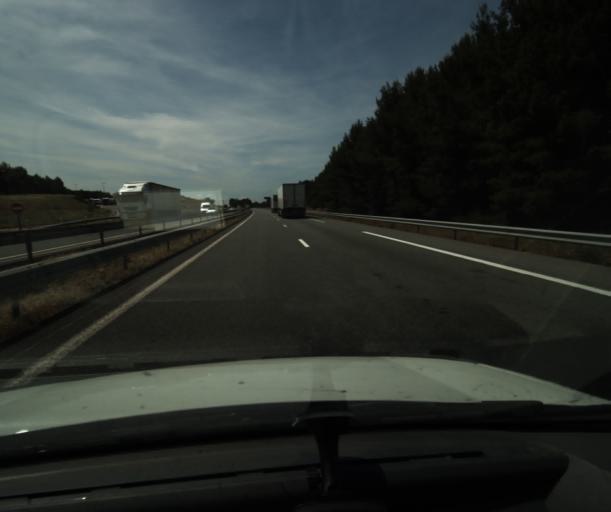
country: FR
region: Languedoc-Roussillon
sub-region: Departement de l'Aude
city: Arzens
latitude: 43.2172
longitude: 2.2240
